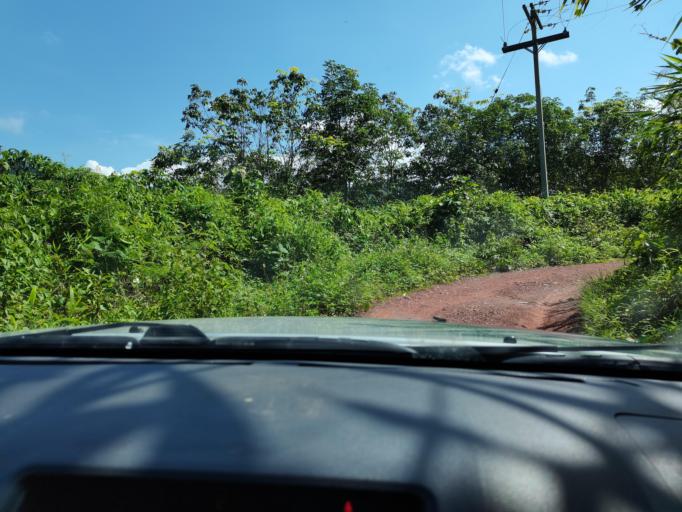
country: LA
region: Loungnamtha
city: Muang Nale
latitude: 20.5578
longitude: 101.0582
